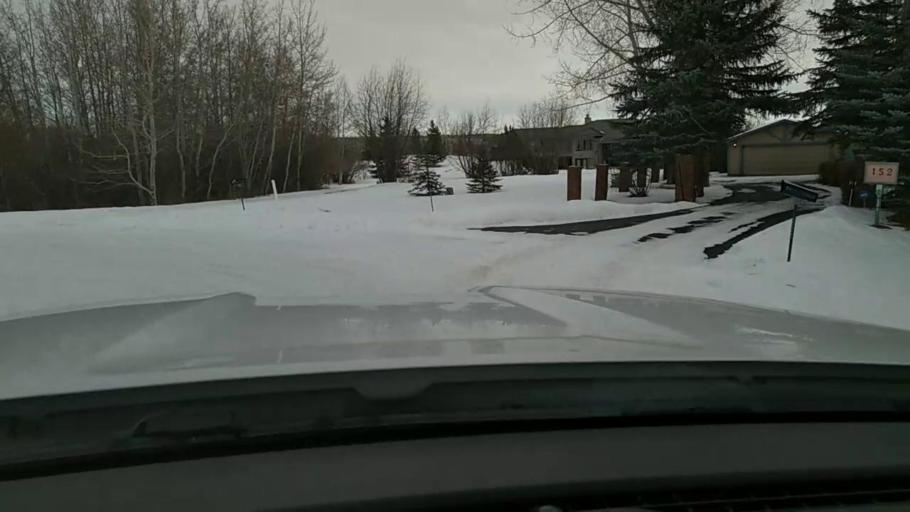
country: CA
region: Alberta
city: Calgary
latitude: 51.1190
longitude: -114.2667
